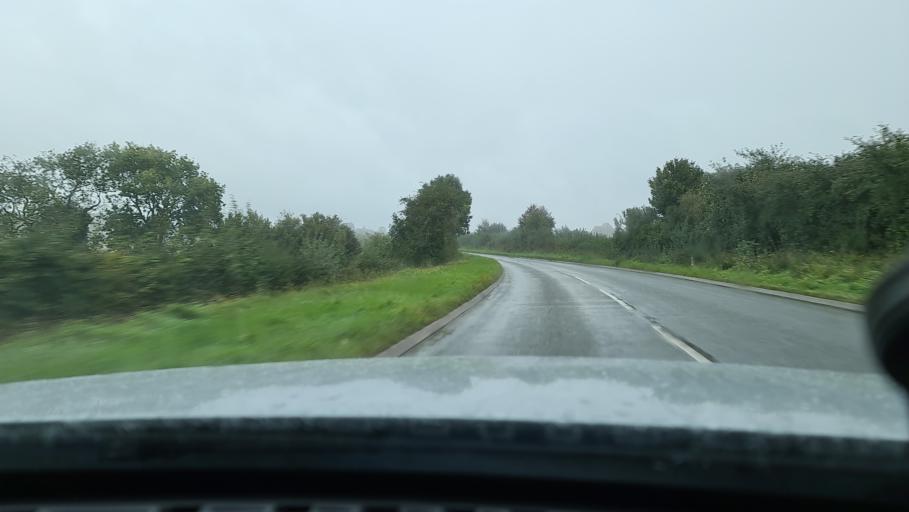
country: GB
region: England
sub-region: Oxfordshire
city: Somerton
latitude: 51.9232
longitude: -1.2797
